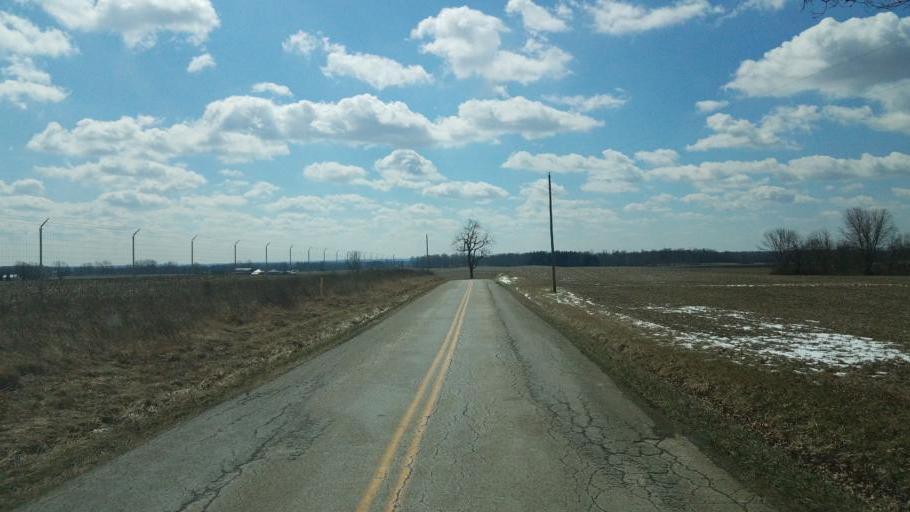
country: US
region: Ohio
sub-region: Knox County
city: Mount Vernon
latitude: 40.3331
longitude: -82.5430
